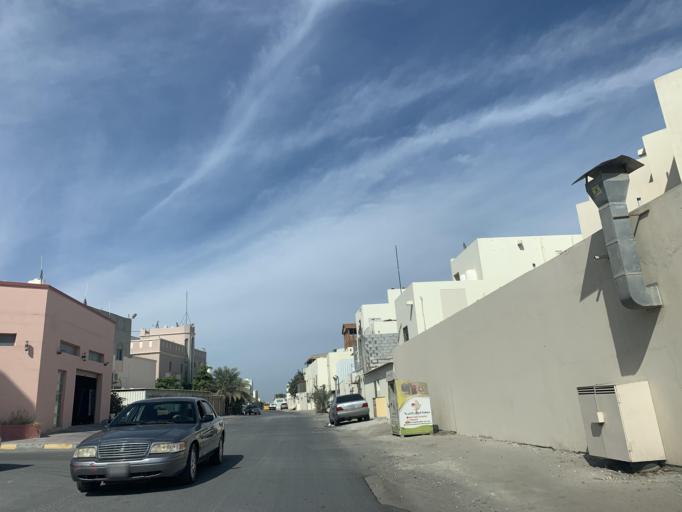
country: BH
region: Central Governorate
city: Madinat Hamad
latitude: 26.1193
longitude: 50.4815
